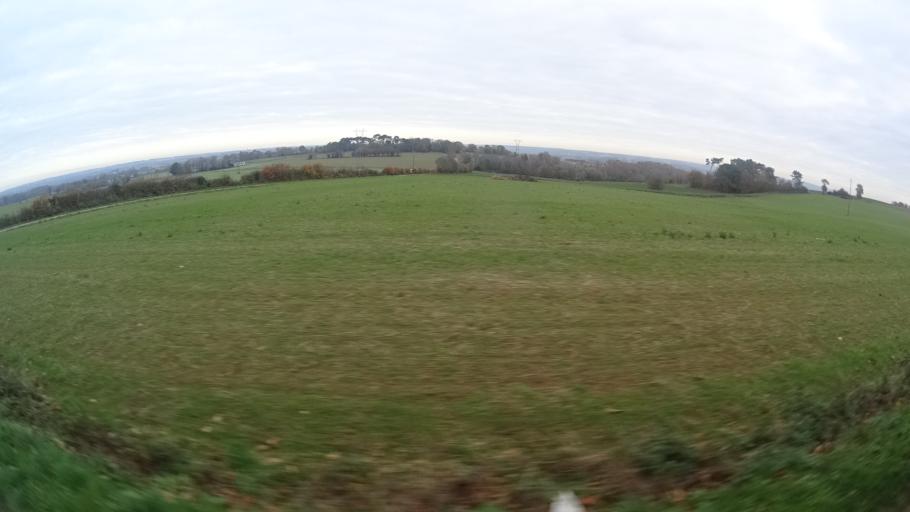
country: FR
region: Pays de la Loire
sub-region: Departement de la Loire-Atlantique
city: Avessac
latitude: 47.6536
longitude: -1.9650
